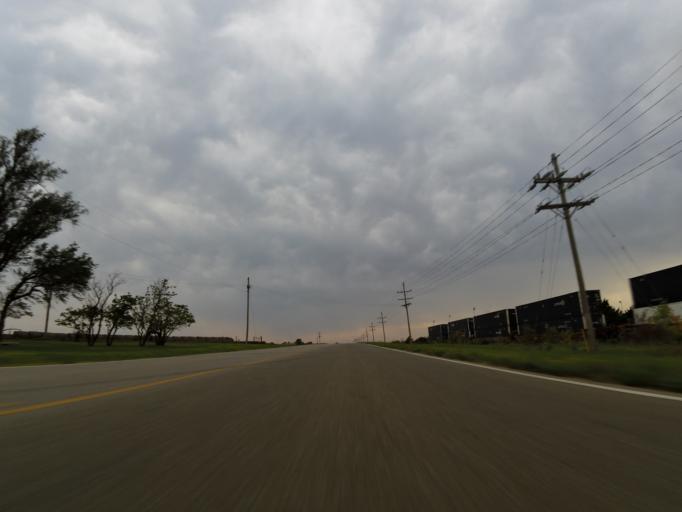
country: US
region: Kansas
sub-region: Reno County
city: South Hutchinson
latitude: 38.0213
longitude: -97.9890
